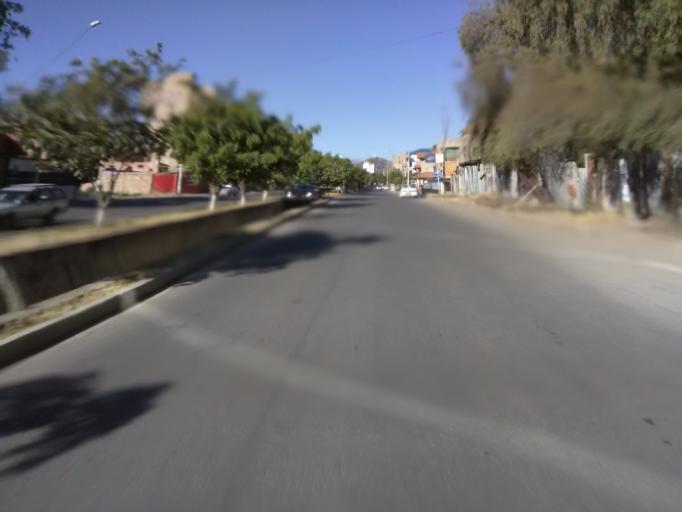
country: BO
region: Cochabamba
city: Cochabamba
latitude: -17.3827
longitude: -66.1896
